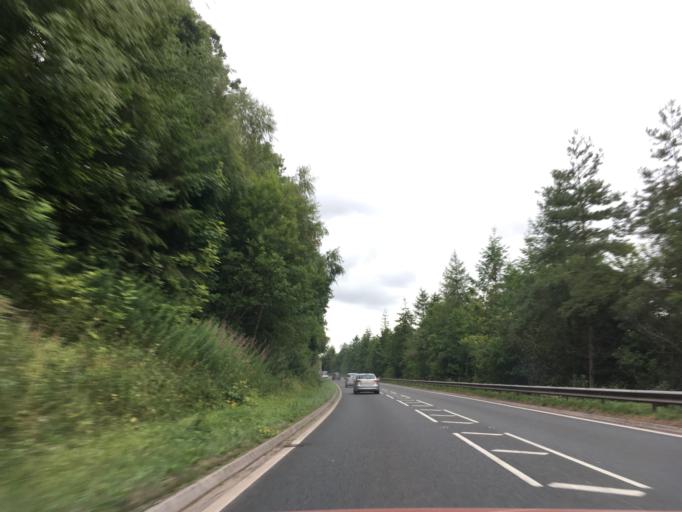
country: GB
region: Wales
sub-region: Sir Powys
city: Brecon
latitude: 51.9535
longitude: -3.4590
